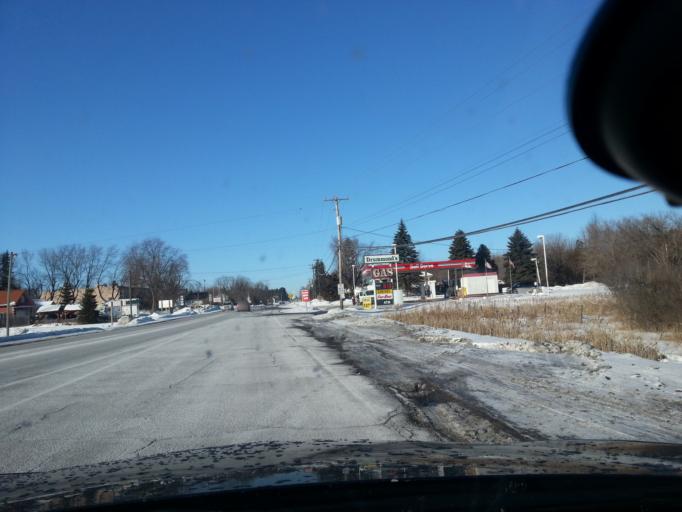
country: CA
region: Ontario
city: Ottawa
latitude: 45.2807
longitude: -75.5706
